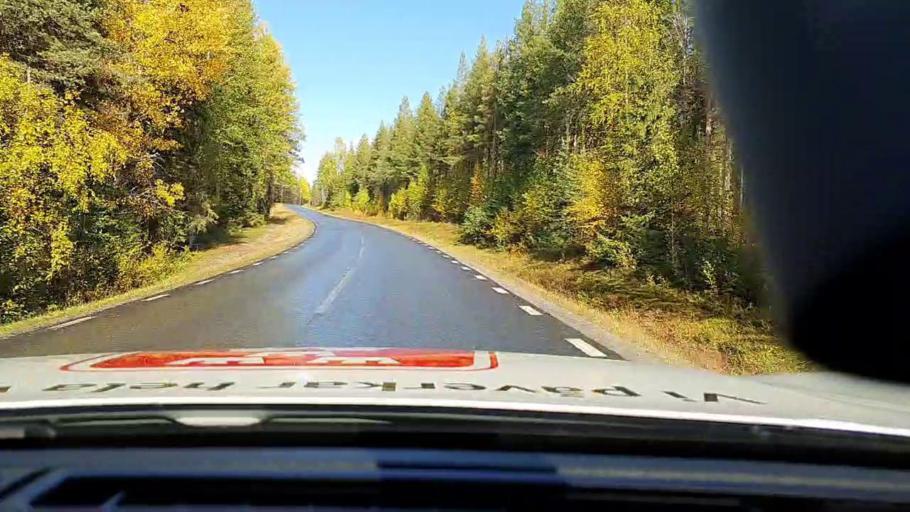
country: SE
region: Vaesterbotten
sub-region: Skelleftea Kommun
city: Langsele
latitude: 64.9627
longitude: 20.0441
